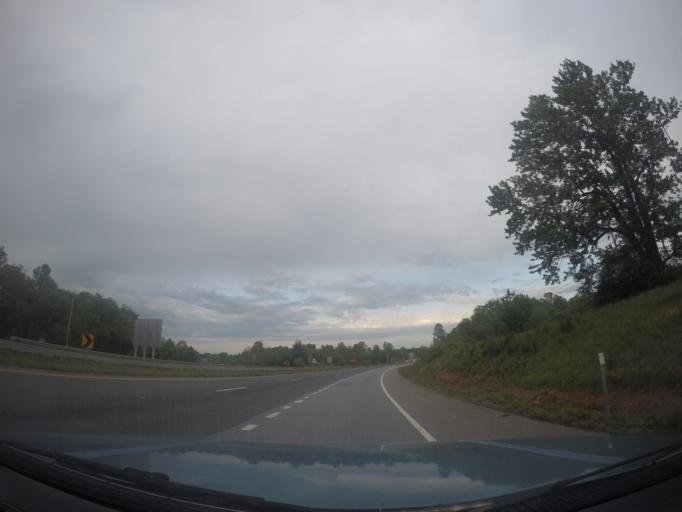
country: US
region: Virginia
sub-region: City of Lynchburg
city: Lynchburg
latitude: 37.3862
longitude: -79.1047
